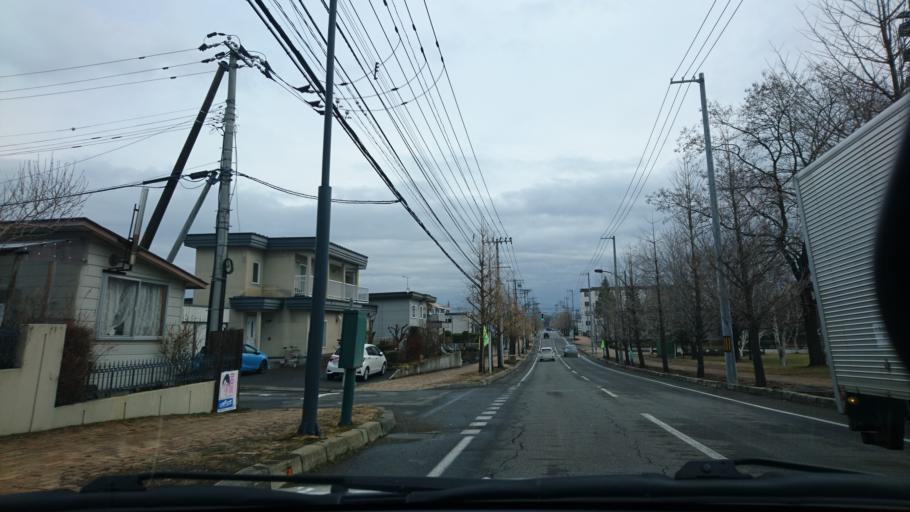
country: JP
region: Hokkaido
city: Otofuke
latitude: 42.9622
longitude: 143.2029
